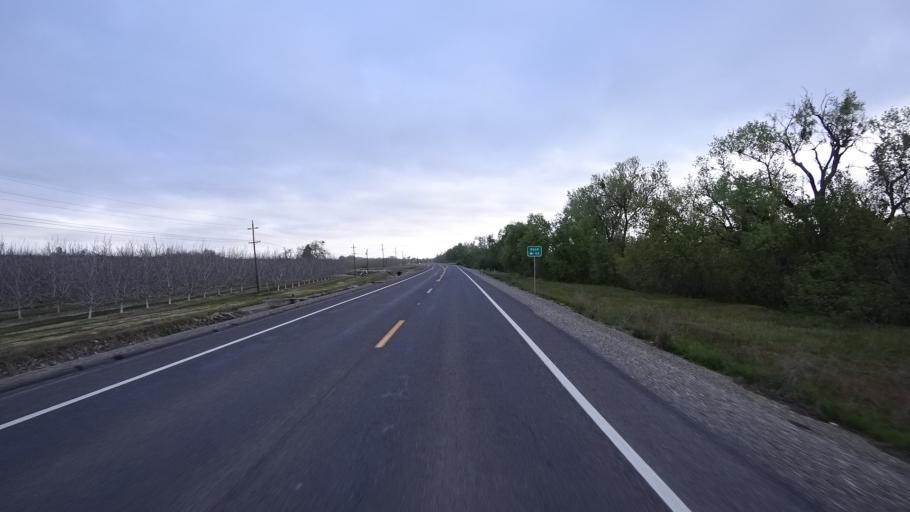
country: US
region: California
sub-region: Glenn County
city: Willows
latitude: 39.4260
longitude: -122.0113
